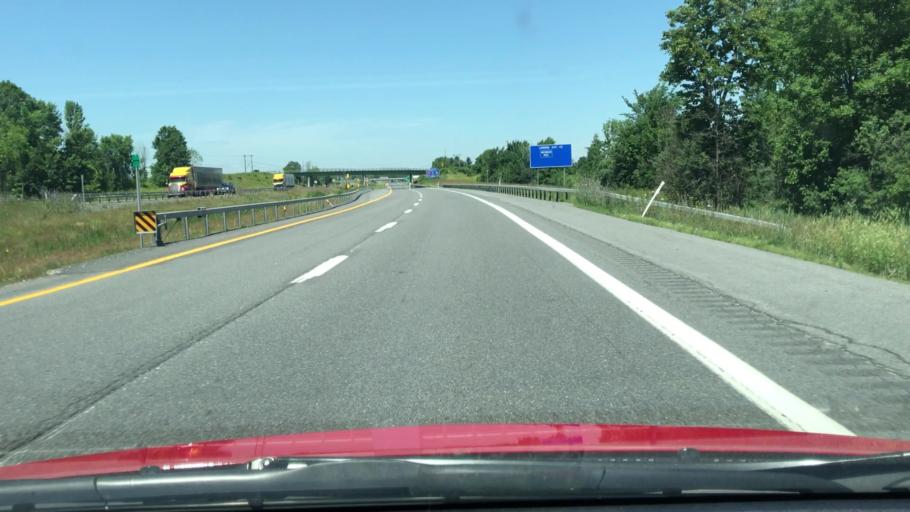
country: US
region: New York
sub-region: Clinton County
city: Champlain
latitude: 44.9700
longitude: -73.4509
